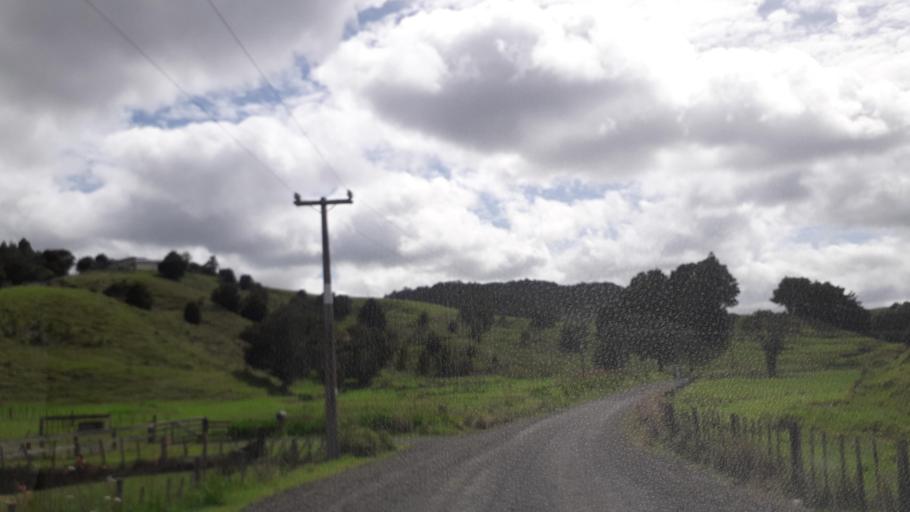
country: NZ
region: Northland
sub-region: Far North District
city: Ahipara
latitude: -35.2411
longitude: 173.2558
